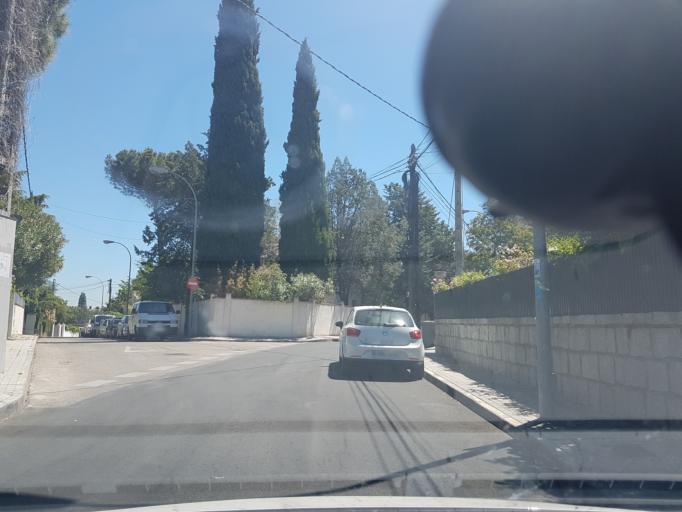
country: ES
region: Madrid
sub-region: Provincia de Madrid
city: Pozuelo de Alarcon
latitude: 40.4417
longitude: -3.8111
